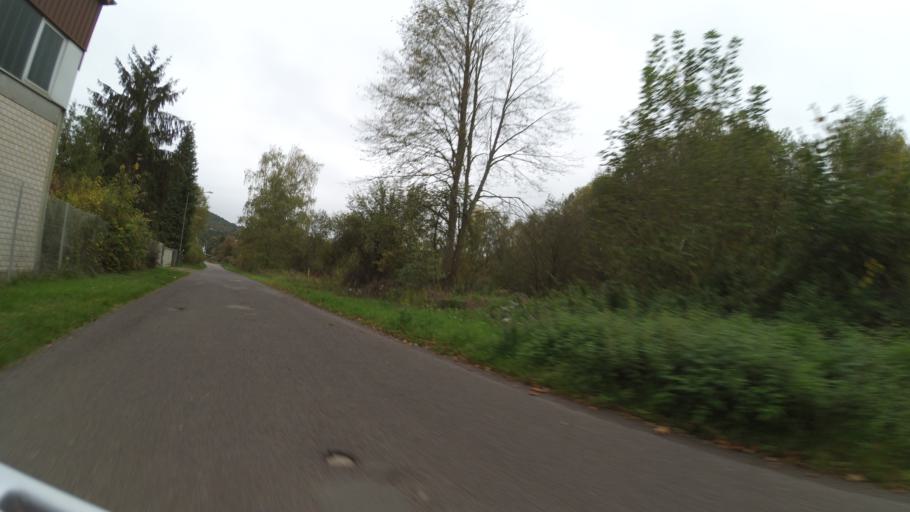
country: DE
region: Saarland
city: Homburg
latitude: 49.3035
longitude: 7.3179
